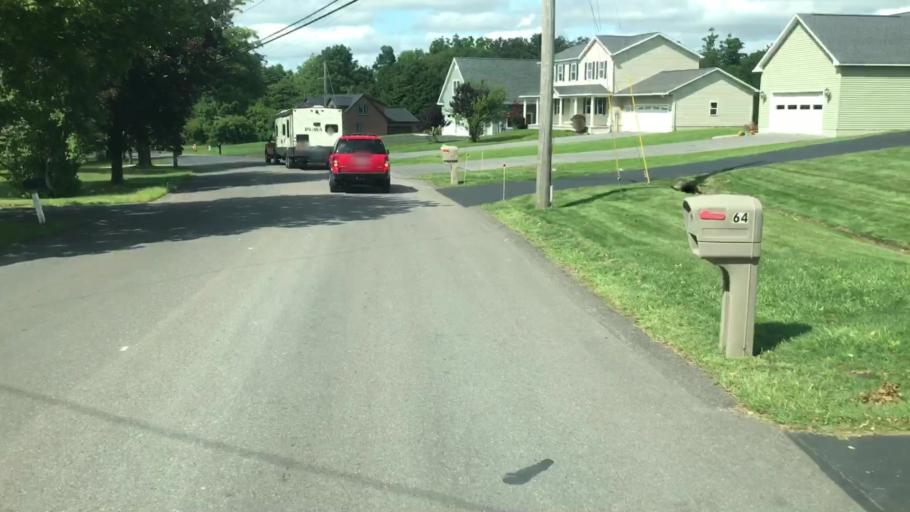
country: US
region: New York
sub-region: Cayuga County
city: Auburn
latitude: 42.9508
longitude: -76.5406
